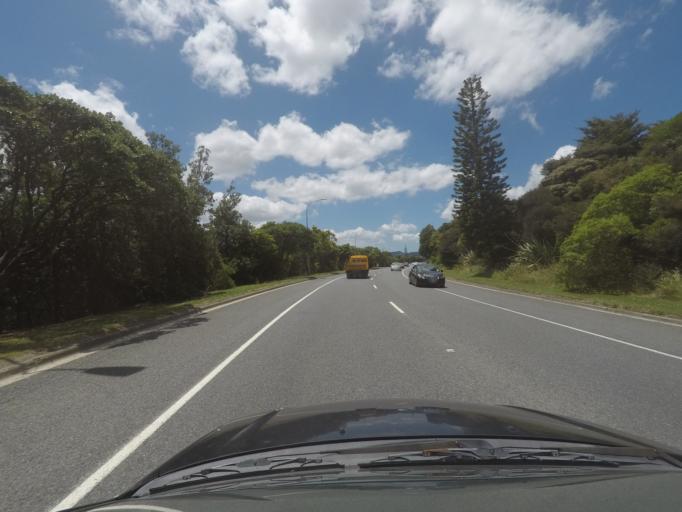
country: NZ
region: Northland
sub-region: Whangarei
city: Whangarei
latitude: -35.7465
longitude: 174.3216
